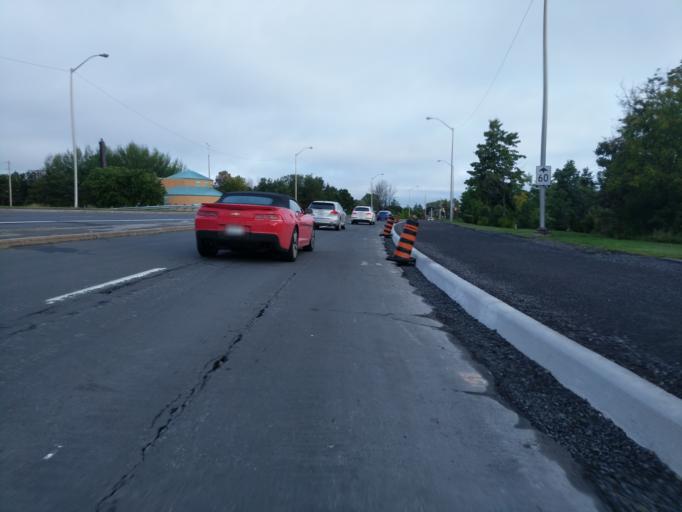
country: CA
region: Ontario
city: Bells Corners
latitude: 45.3452
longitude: -75.8153
